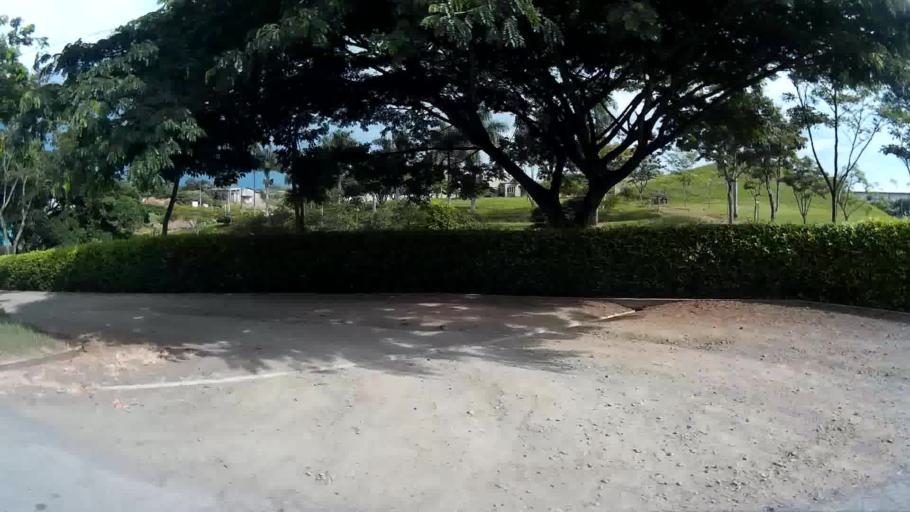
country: CO
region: Valle del Cauca
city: Cartago
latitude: 4.8030
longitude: -75.8310
